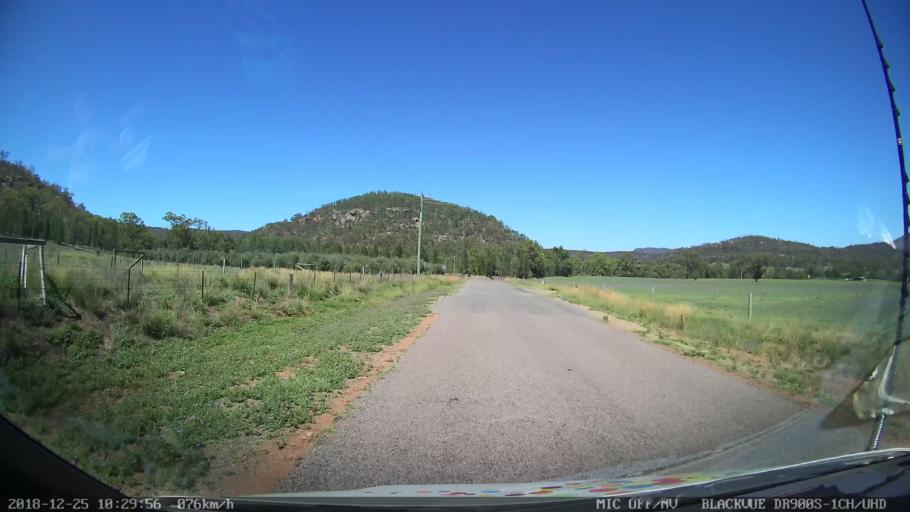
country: AU
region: New South Wales
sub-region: Muswellbrook
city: Denman
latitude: -32.3812
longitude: 150.4445
